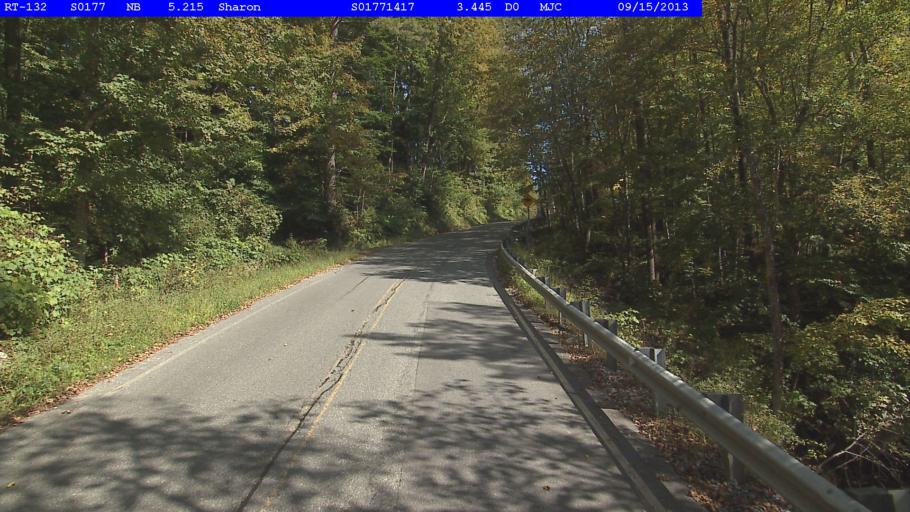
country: US
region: Vermont
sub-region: Windsor County
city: Woodstock
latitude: 43.7885
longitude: -72.4499
